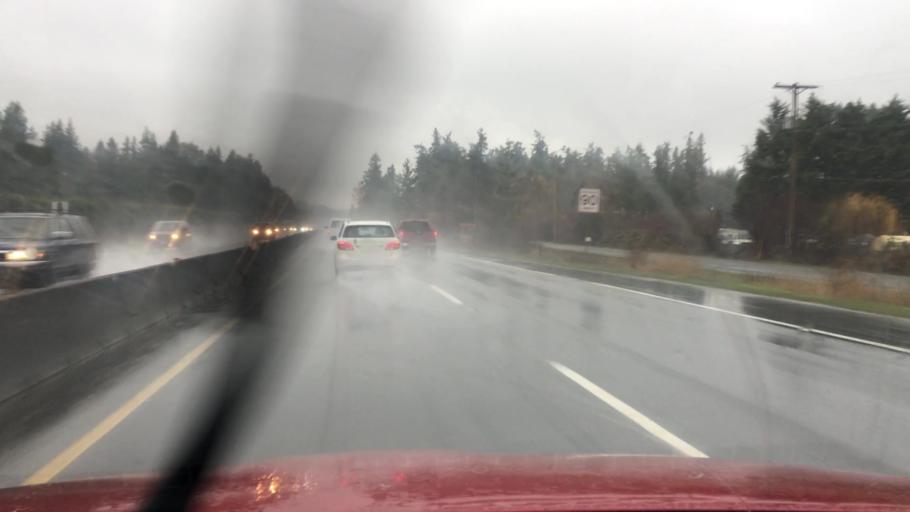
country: CA
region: British Columbia
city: North Saanich
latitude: 48.5767
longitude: -123.3978
